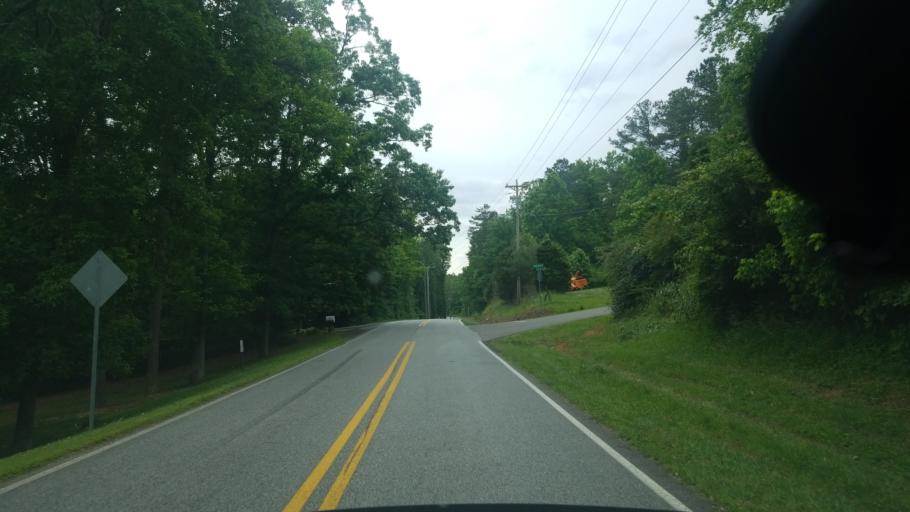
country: US
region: Georgia
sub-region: Forsyth County
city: Cumming
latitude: 34.1587
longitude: -84.1280
